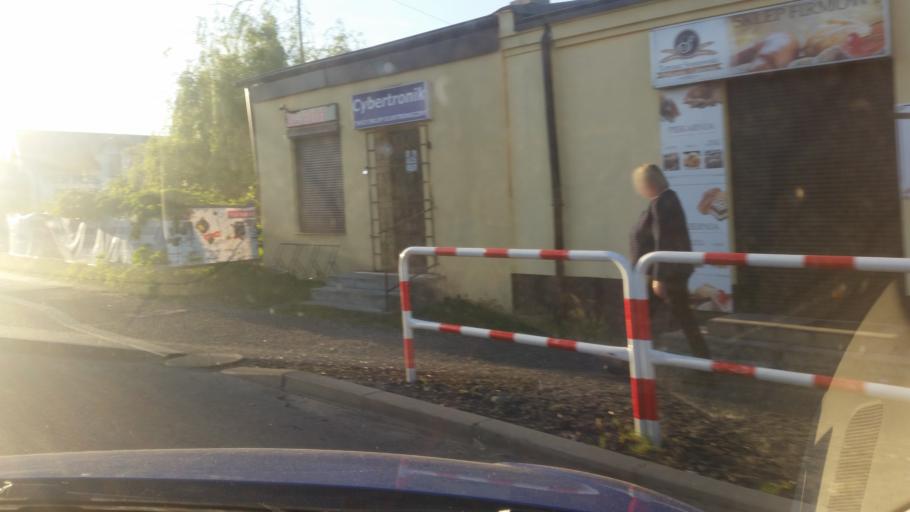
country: PL
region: Silesian Voivodeship
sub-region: Powiat czestochowski
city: Klomnice
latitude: 50.9218
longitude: 19.3568
